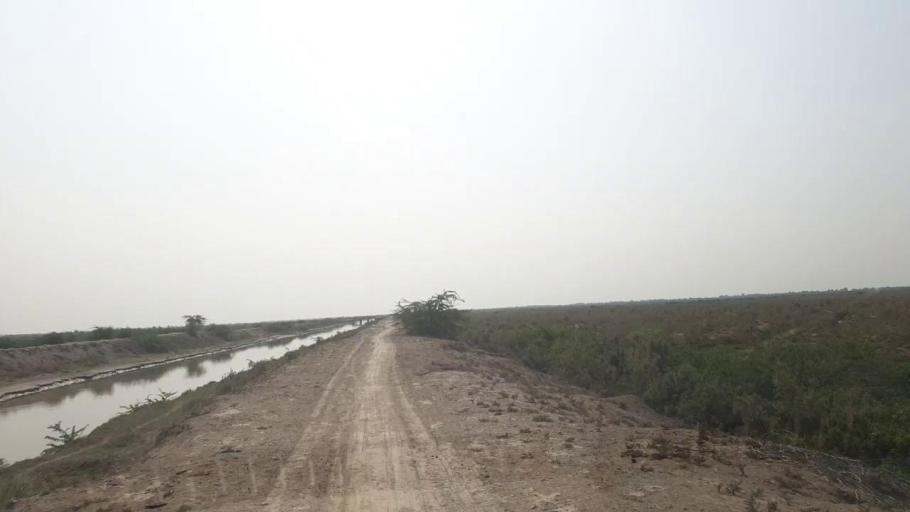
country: PK
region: Sindh
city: Kadhan
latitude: 24.3843
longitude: 68.8994
